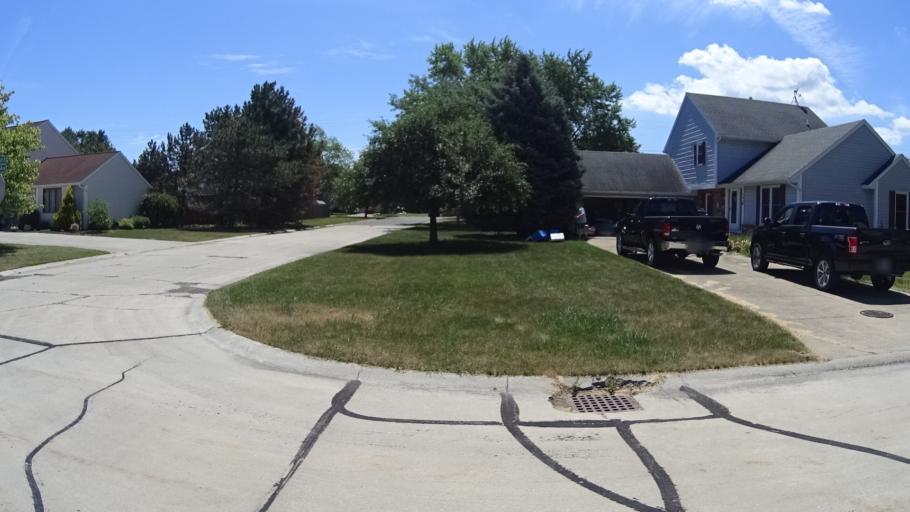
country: US
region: Ohio
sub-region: Erie County
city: Sandusky
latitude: 41.4071
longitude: -82.6890
